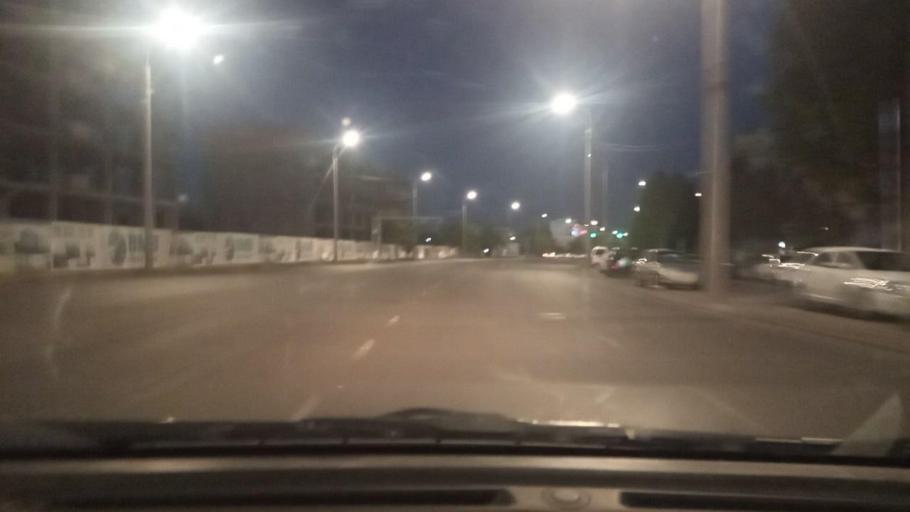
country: UZ
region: Toshkent Shahri
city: Tashkent
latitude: 41.2668
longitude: 69.2485
